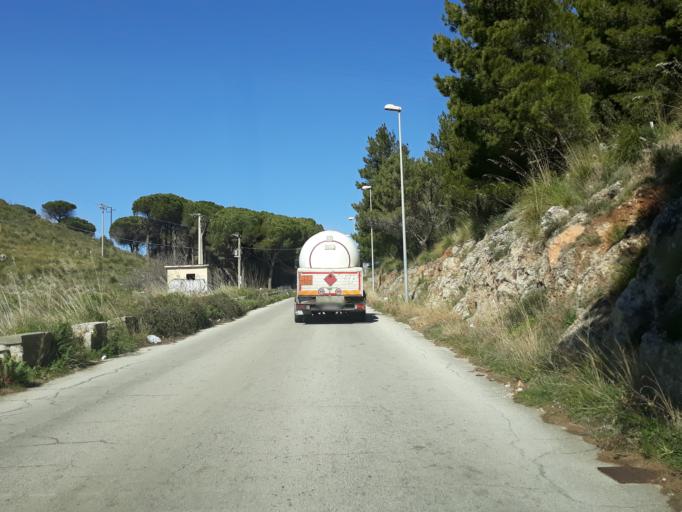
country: IT
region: Sicily
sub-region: Palermo
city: Piano dei Geli
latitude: 38.0816
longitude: 13.2720
